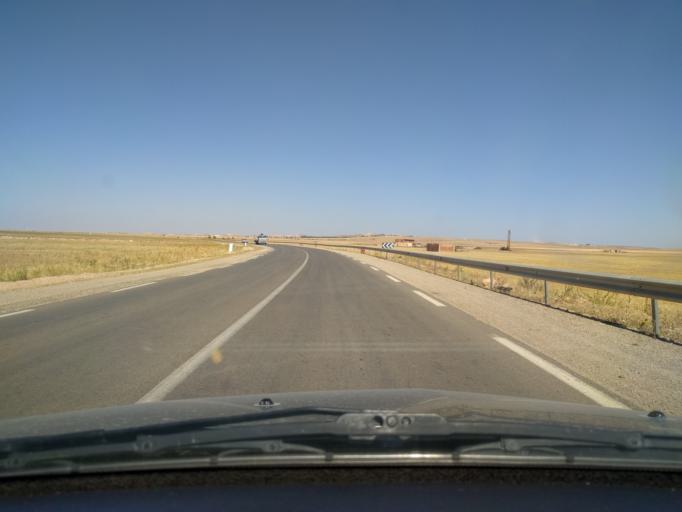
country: DZ
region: Tiaret
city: Frenda
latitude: 34.9047
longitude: 1.1459
